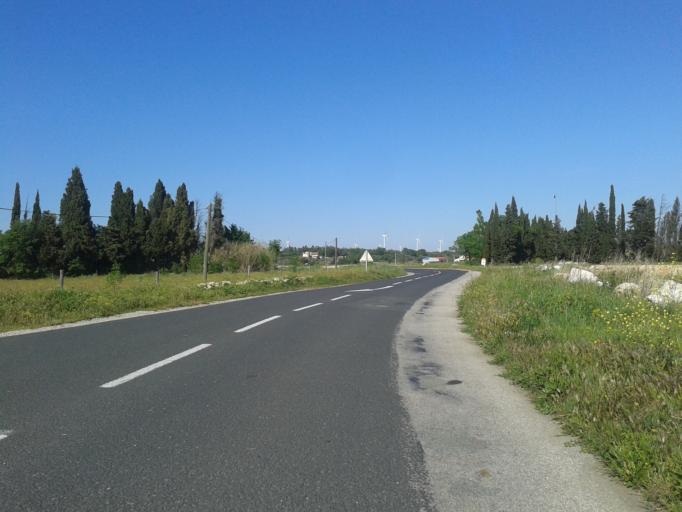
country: FR
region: Languedoc-Roussillon
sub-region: Departement des Pyrenees-Orientales
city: Pezilla-la-Riviere
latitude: 42.6970
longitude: 2.7582
